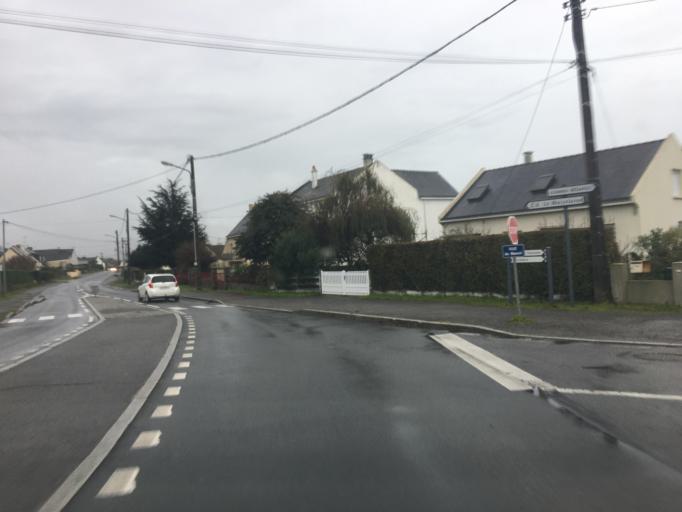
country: FR
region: Pays de la Loire
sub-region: Departement de la Loire-Atlantique
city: La Turballe
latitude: 47.3492
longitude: -2.4870
